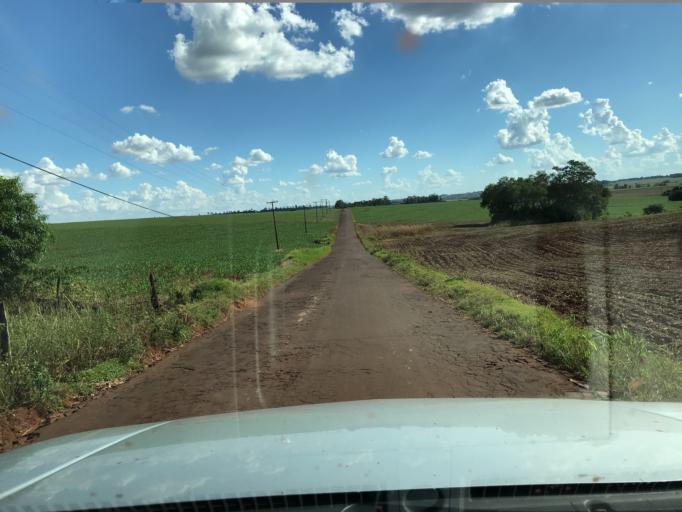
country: BR
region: Parana
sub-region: Palotina
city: Palotina
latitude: -24.2375
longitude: -53.7872
